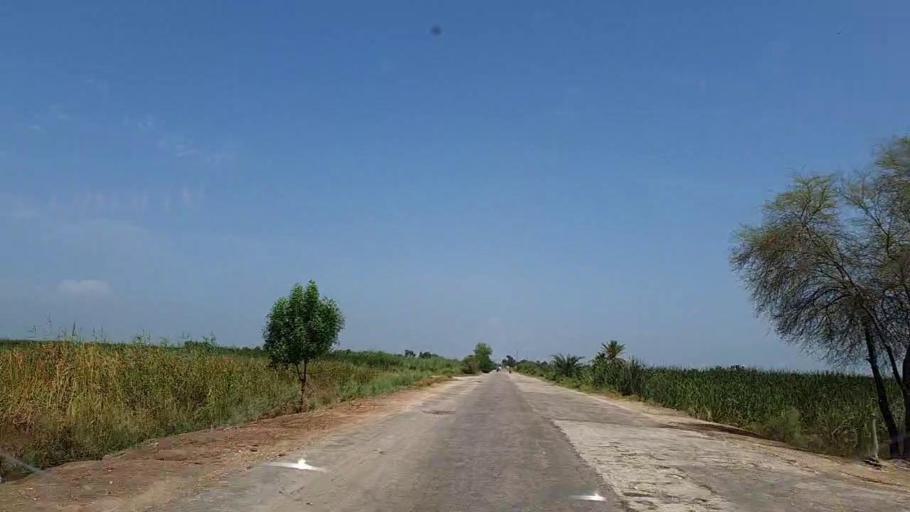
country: PK
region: Sindh
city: Naushahro Firoz
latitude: 26.8164
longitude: 68.1805
